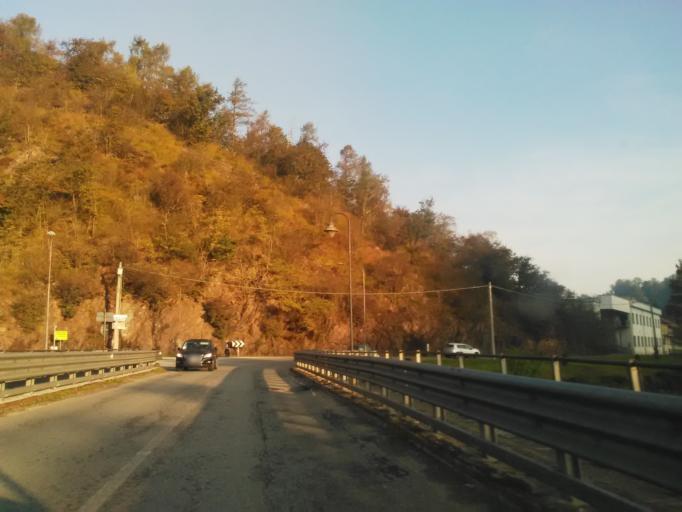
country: IT
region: Piedmont
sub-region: Provincia di Biella
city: Crevacuore
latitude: 45.6826
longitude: 8.2471
